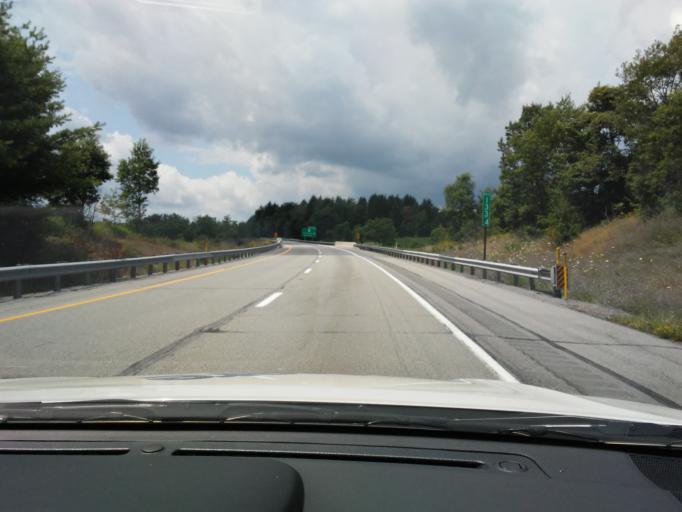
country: US
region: Pennsylvania
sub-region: Clearfield County
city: Troy
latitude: 40.9897
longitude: -78.1594
